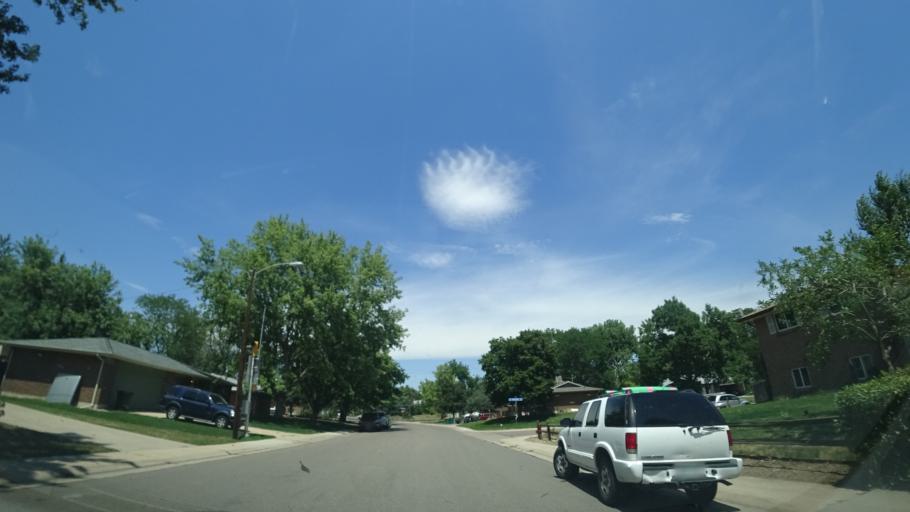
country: US
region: Colorado
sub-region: Jefferson County
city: Lakewood
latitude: 39.6955
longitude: -105.0947
